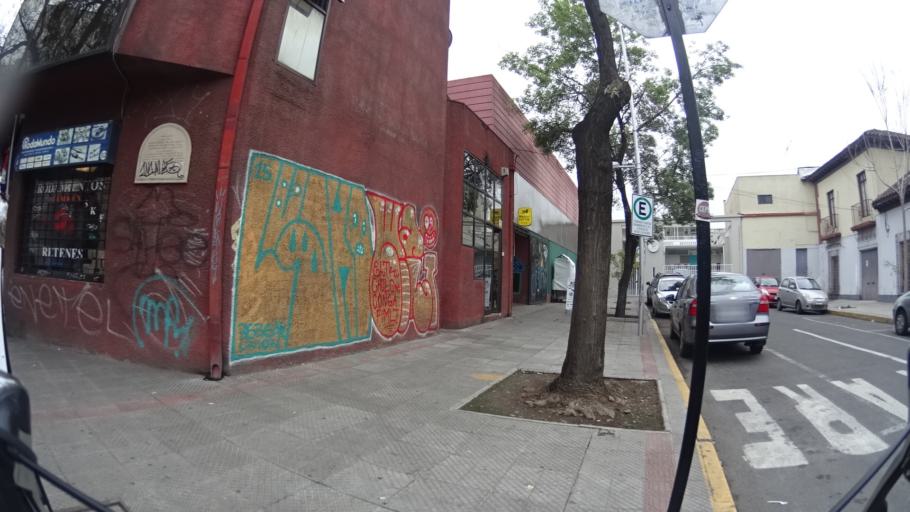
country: CL
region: Santiago Metropolitan
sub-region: Provincia de Santiago
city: Santiago
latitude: -33.4487
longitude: -70.6624
